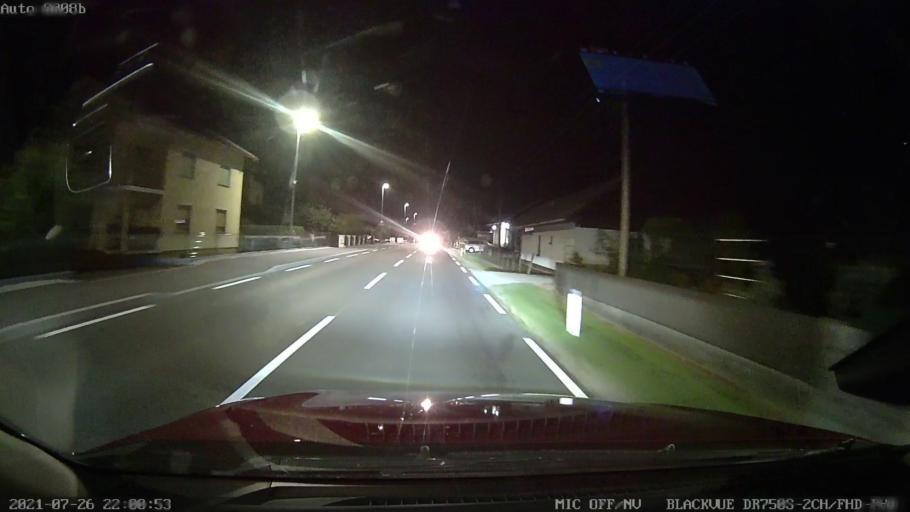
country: SI
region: Markovci
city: Markovci
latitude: 46.3887
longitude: 15.9527
